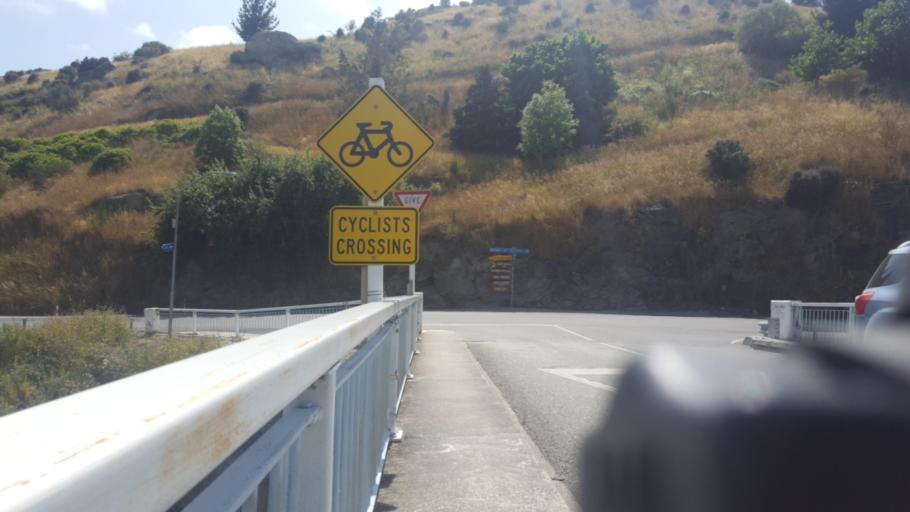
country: NZ
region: Otago
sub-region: Queenstown-Lakes District
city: Kingston
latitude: -45.5423
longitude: 169.3207
